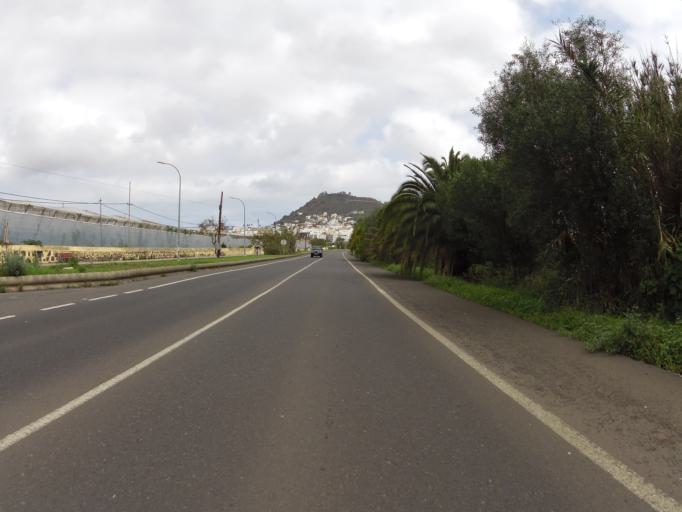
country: ES
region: Canary Islands
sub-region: Provincia de Las Palmas
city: Arucas
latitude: 28.1105
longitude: -15.5260
